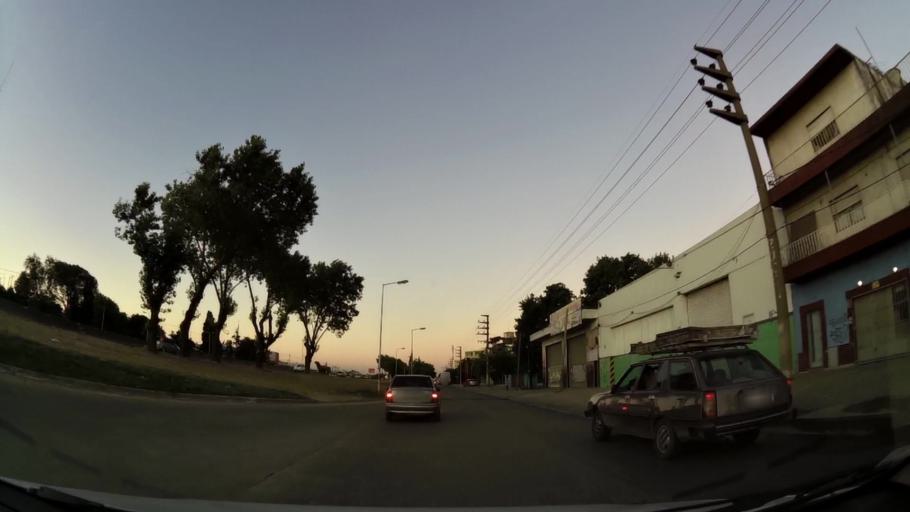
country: AR
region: Buenos Aires
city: San Justo
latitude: -34.7230
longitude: -58.5975
